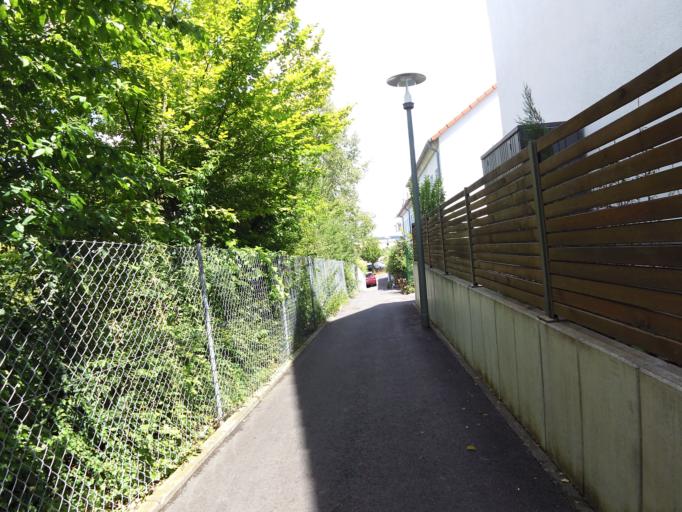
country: DE
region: Bavaria
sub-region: Regierungsbezirk Unterfranken
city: Estenfeld
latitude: 49.8064
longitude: 9.9891
